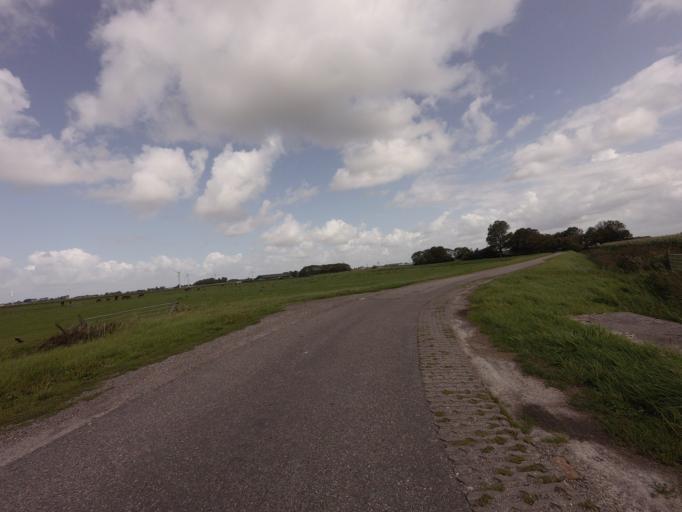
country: NL
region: Friesland
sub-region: Gemeente Franekeradeel
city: Sexbierum
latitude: 53.1696
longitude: 5.4862
